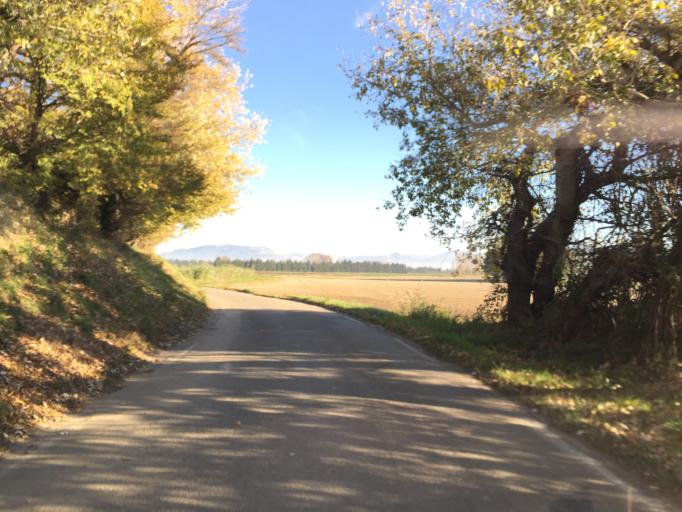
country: FR
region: Provence-Alpes-Cote d'Azur
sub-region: Departement du Vaucluse
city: Bedarrides
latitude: 44.0580
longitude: 4.9310
